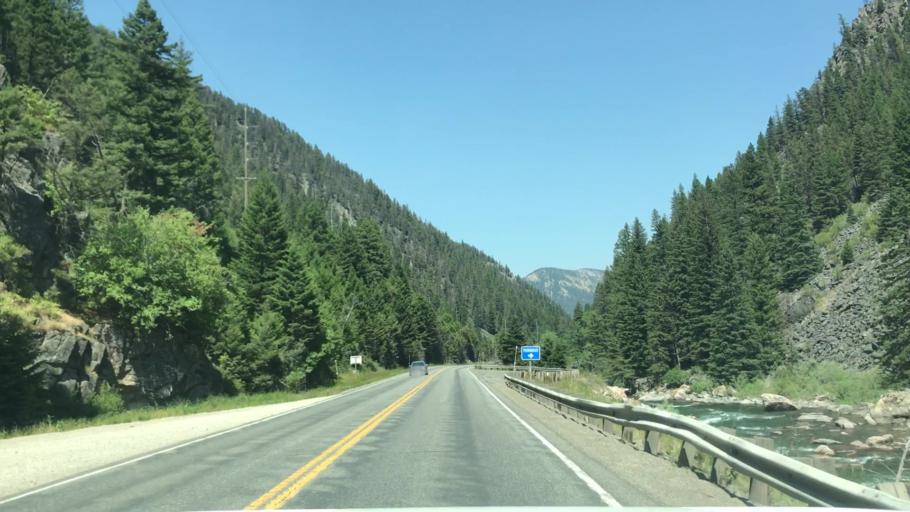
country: US
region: Montana
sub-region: Gallatin County
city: Big Sky
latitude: 45.4183
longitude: -111.2333
